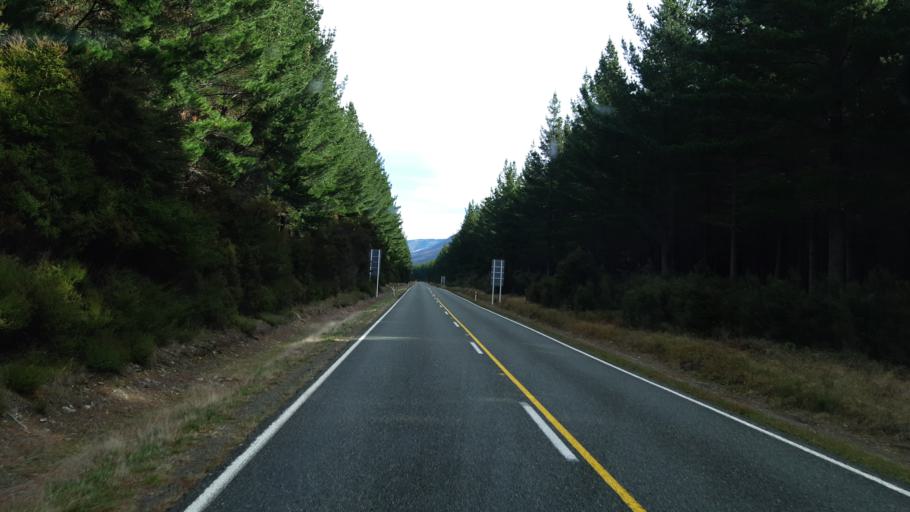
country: NZ
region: Tasman
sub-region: Tasman District
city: Wakefield
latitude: -41.7172
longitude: 173.0763
